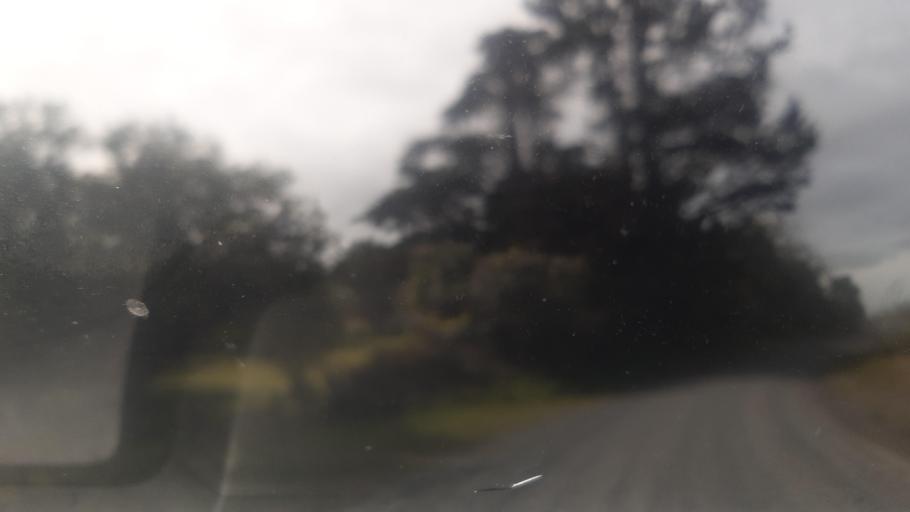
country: NZ
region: Northland
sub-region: Far North District
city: Kaitaia
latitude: -35.0250
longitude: 173.2218
